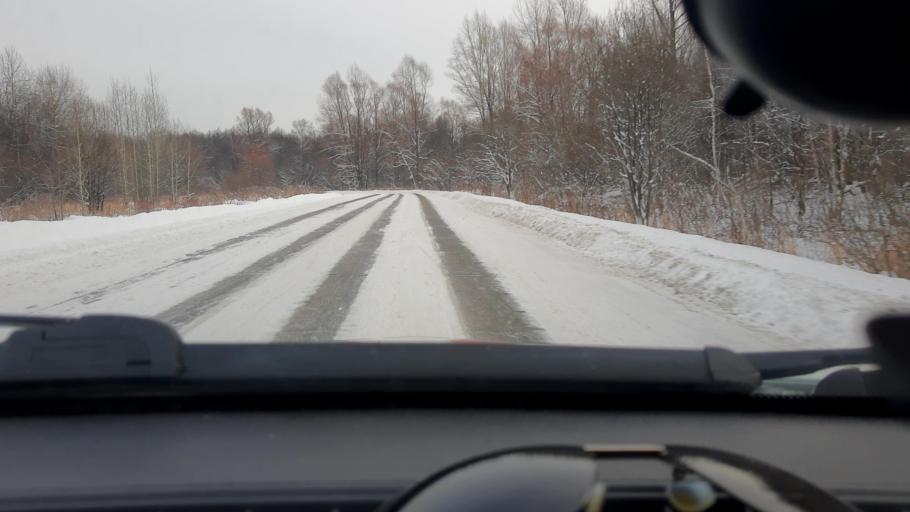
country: RU
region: Bashkortostan
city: Blagoveshchensk
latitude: 55.0314
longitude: 56.1059
